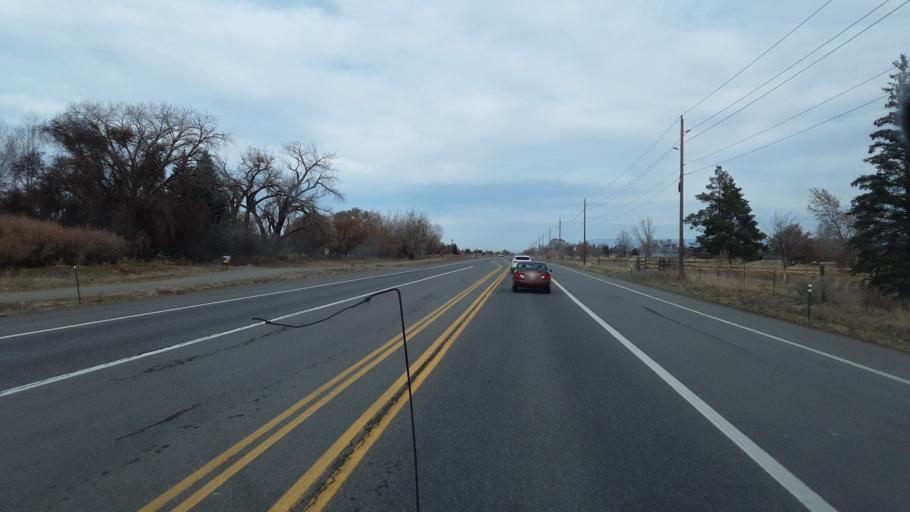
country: US
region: Colorado
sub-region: Montrose County
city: Montrose
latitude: 38.3670
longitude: -107.8092
